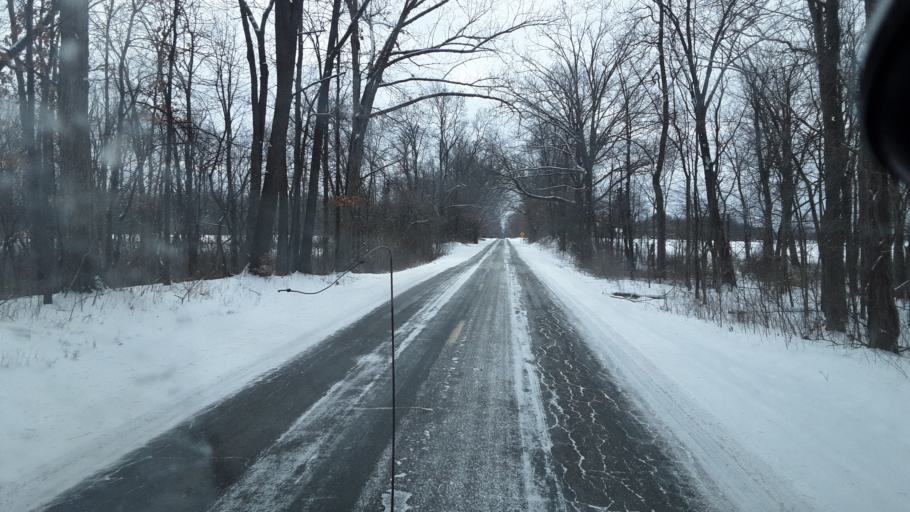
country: US
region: Michigan
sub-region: Ingham County
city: Leslie
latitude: 42.5051
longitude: -84.3892
